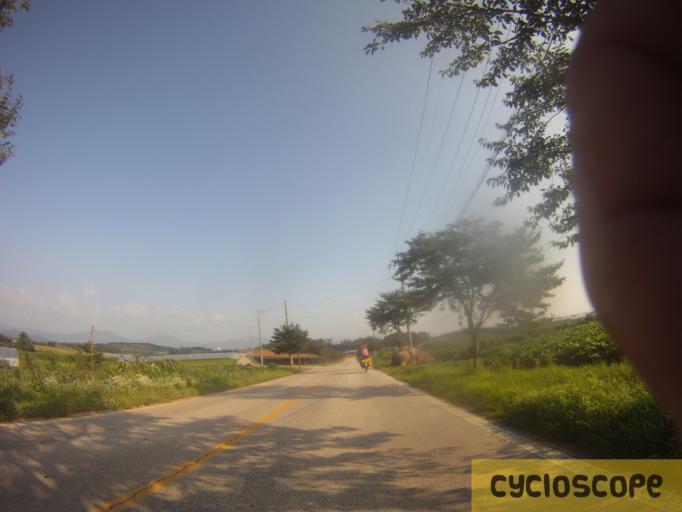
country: KR
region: Jeollabuk-do
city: Koch'ang
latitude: 35.4348
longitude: 126.6474
